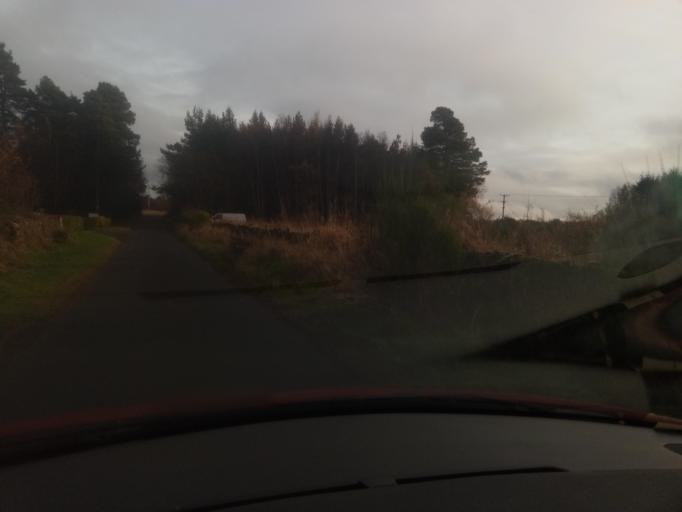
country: GB
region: Scotland
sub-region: The Scottish Borders
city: Jedburgh
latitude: 55.4817
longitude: -2.5760
